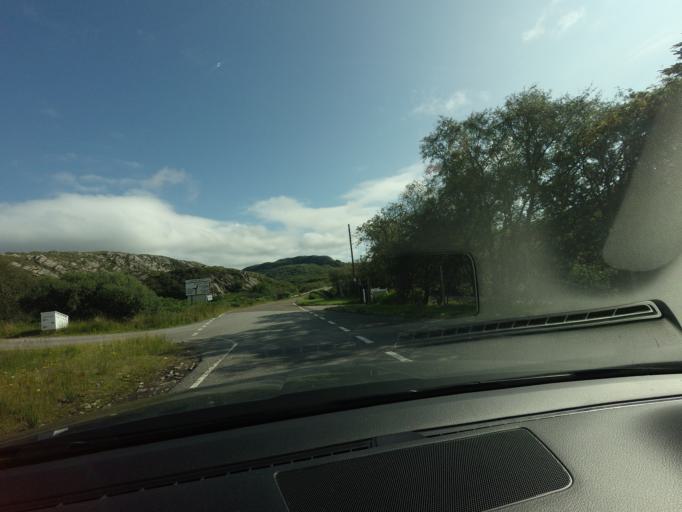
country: GB
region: Scotland
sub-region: Highland
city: Ullapool
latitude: 58.3757
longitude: -5.0169
